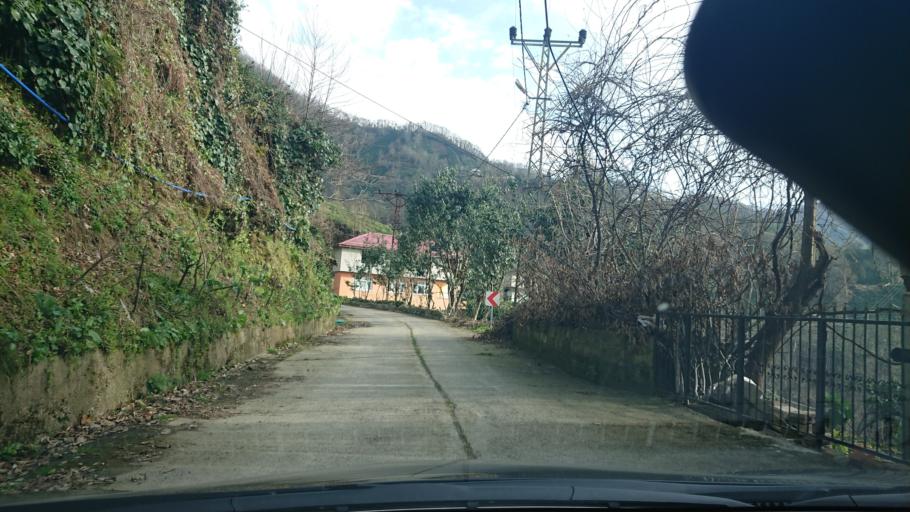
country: TR
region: Rize
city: Rize
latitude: 40.9890
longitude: 40.4919
